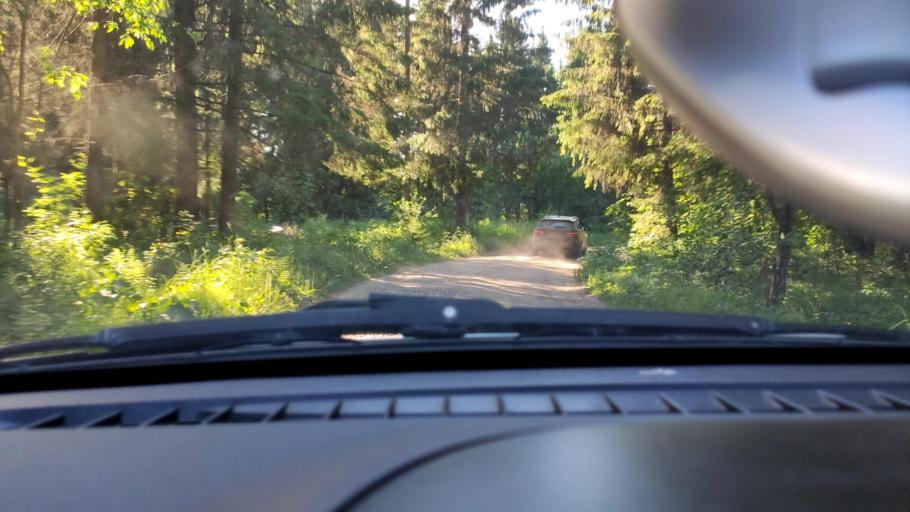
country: RU
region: Perm
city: Bershet'
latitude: 57.6988
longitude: 56.4071
